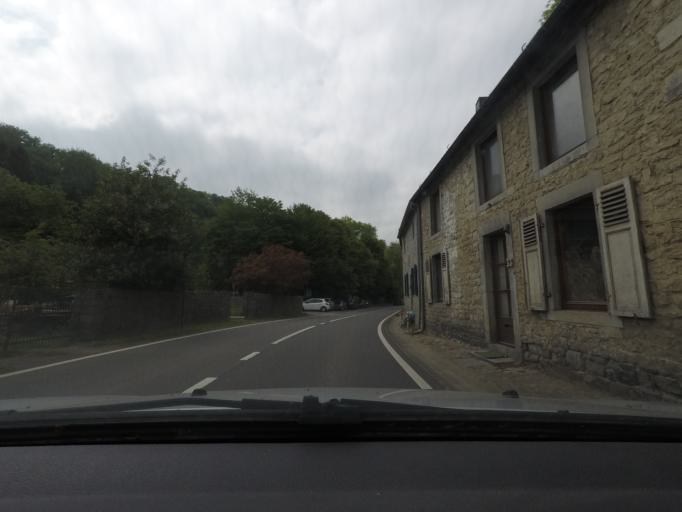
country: BE
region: Wallonia
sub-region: Province de Namur
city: Assesse
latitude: 50.4442
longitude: 5.0101
